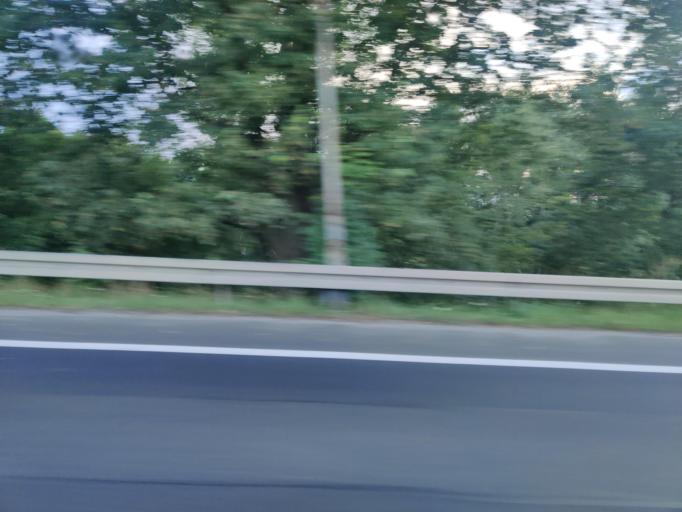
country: PL
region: Greater Poland Voivodeship
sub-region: Konin
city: Konin
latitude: 52.2078
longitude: 18.2654
